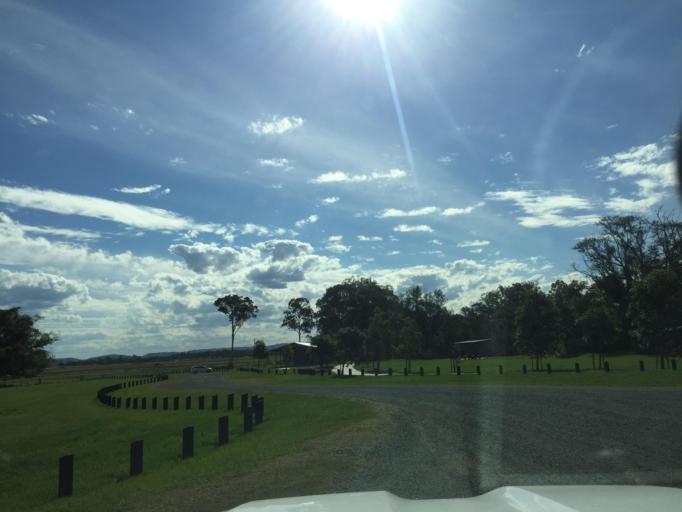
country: AU
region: Queensland
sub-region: Moreton Bay
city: Morayfield
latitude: -27.1060
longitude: 152.9951
